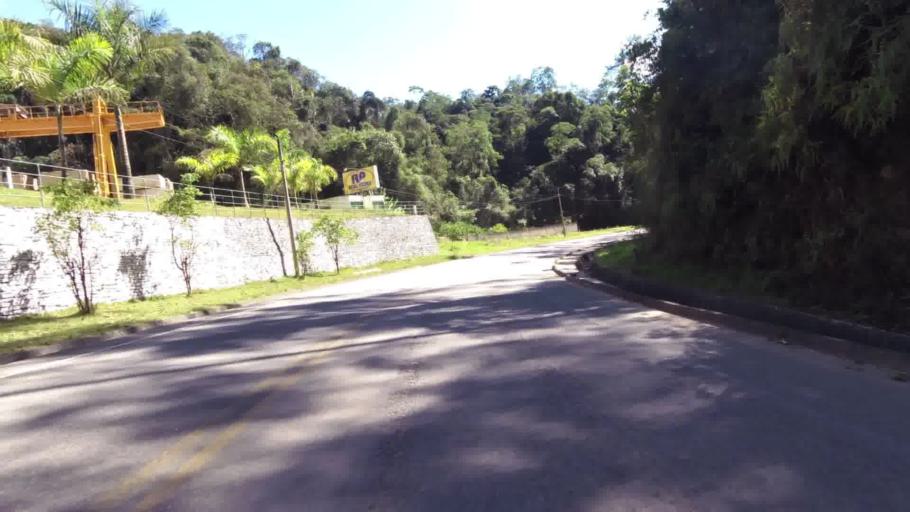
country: BR
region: Espirito Santo
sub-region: Vargem Alta
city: Vargem Alta
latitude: -20.6646
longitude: -40.9622
